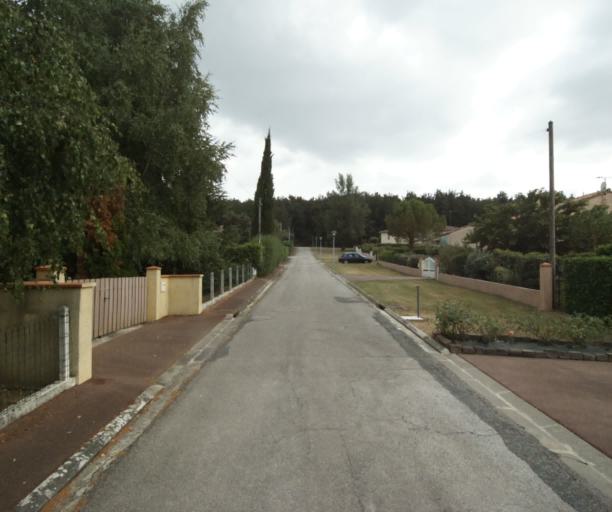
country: FR
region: Midi-Pyrenees
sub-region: Departement de la Haute-Garonne
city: Revel
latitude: 43.4321
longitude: 2.0214
